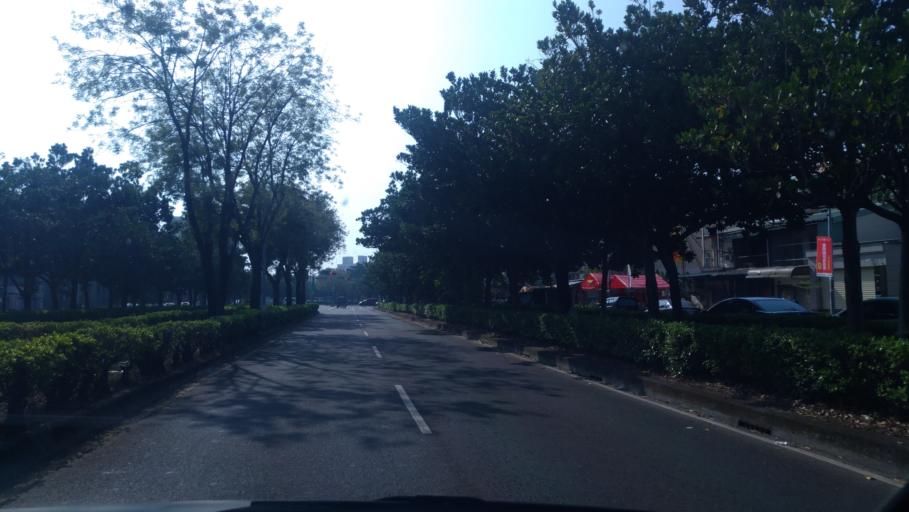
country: TW
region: Taiwan
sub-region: Chiayi
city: Jiayi Shi
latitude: 23.4904
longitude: 120.4429
